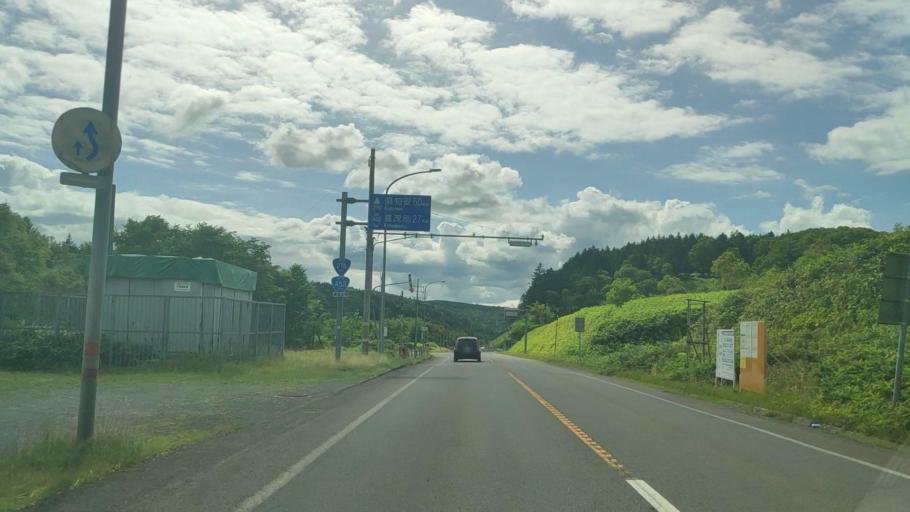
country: JP
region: Hokkaido
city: Shiraoi
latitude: 42.7051
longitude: 141.1737
